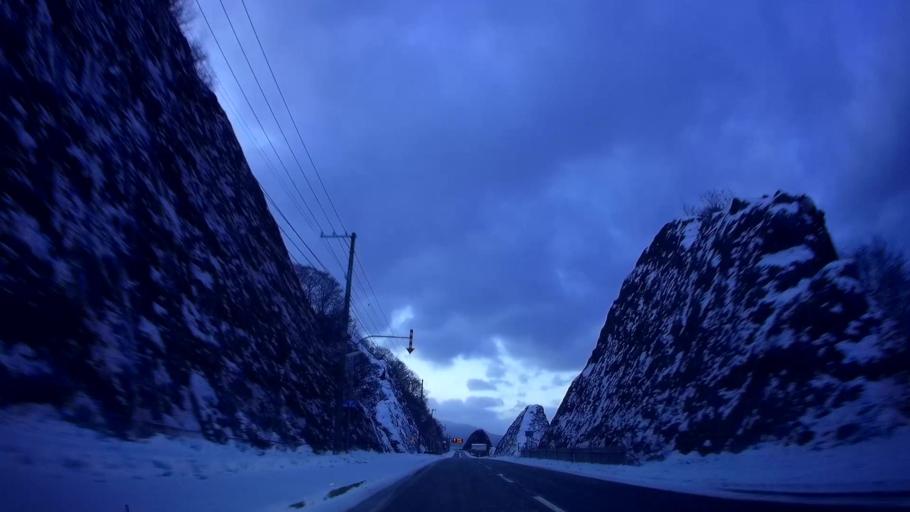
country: JP
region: Hokkaido
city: Hakodate
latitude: 41.8913
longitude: 141.0511
